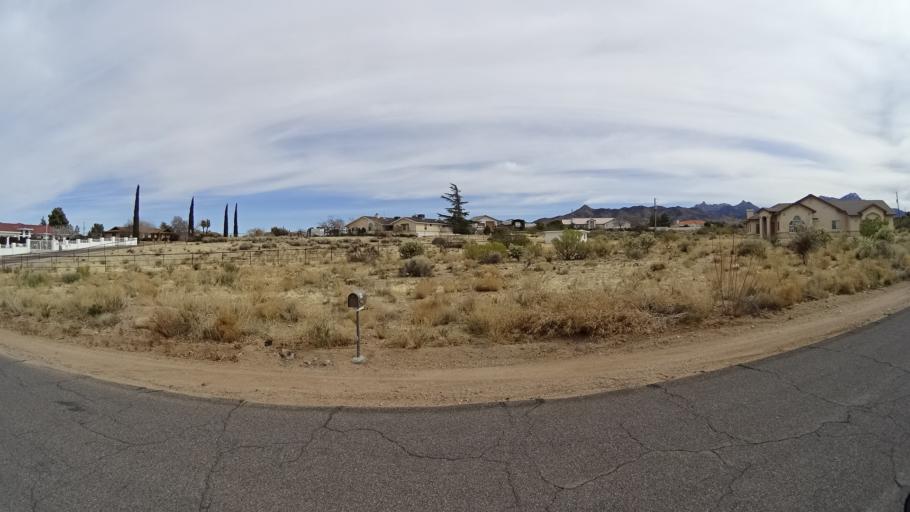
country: US
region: Arizona
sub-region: Mohave County
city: Kingman
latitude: 35.1890
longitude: -113.9928
